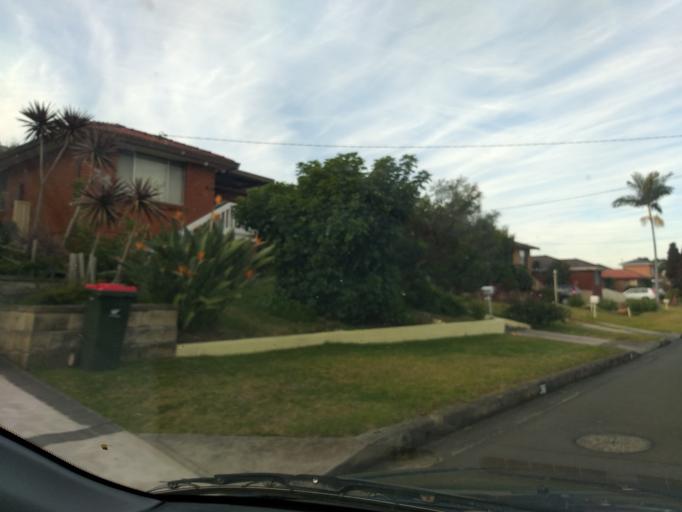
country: AU
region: New South Wales
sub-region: Wollongong
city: Mount Ousley
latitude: -34.3834
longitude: 150.8772
